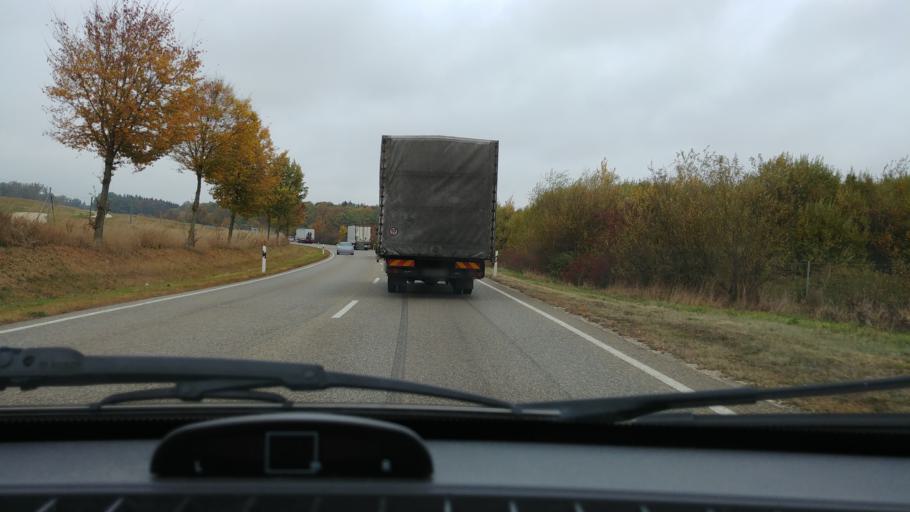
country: DE
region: Baden-Wuerttemberg
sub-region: Regierungsbezirk Stuttgart
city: Aalen
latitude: 48.8448
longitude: 10.0696
